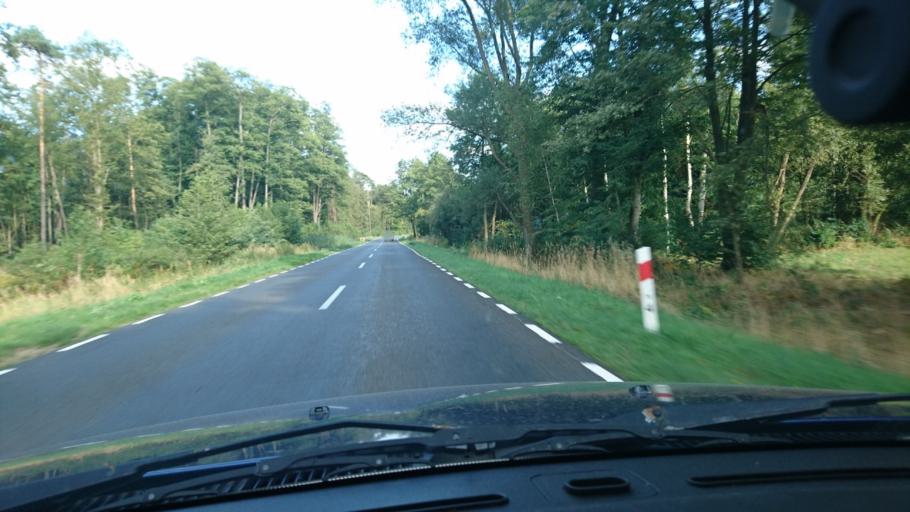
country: PL
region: Greater Poland Voivodeship
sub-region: Powiat krotoszynski
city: Sulmierzyce
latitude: 51.6020
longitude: 17.5859
